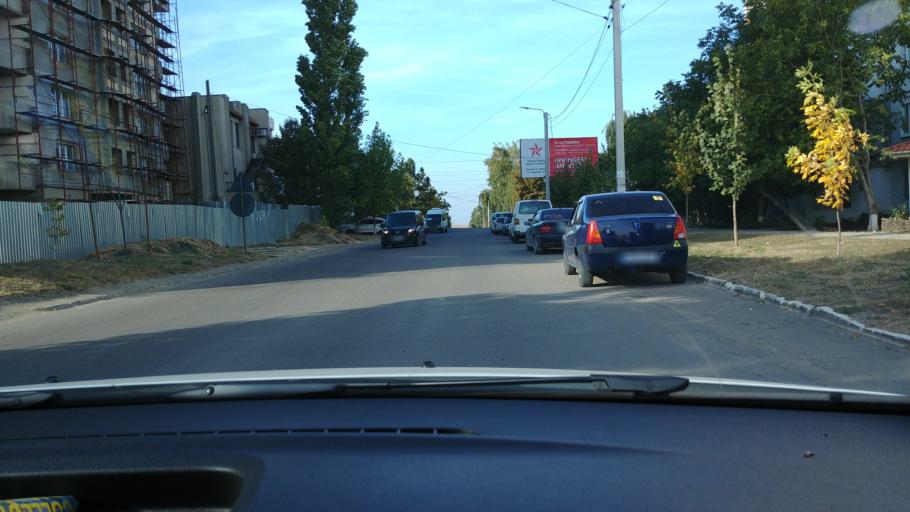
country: MD
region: Rezina
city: Rezina
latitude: 47.7480
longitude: 28.9561
